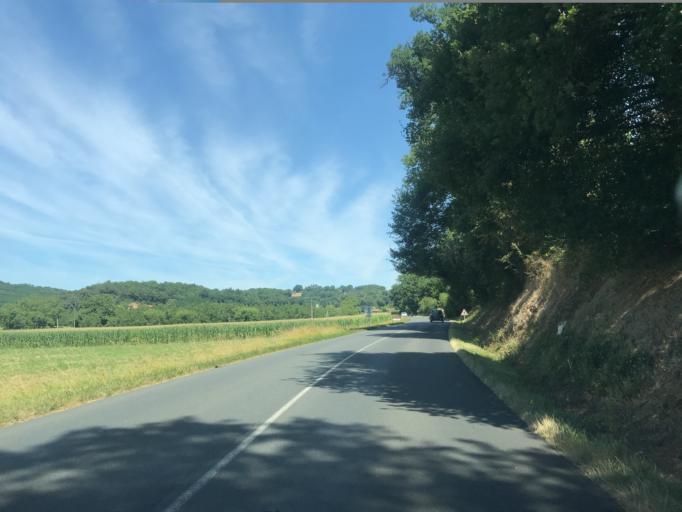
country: FR
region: Aquitaine
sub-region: Departement de la Dordogne
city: Domme
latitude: 44.8197
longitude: 1.2140
